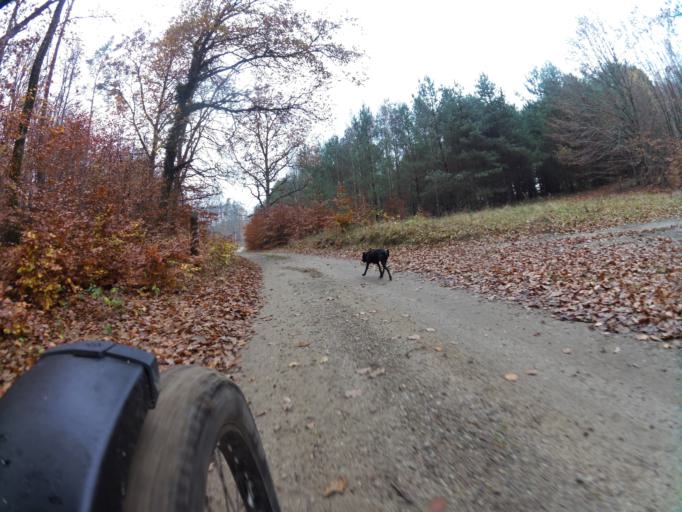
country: PL
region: Pomeranian Voivodeship
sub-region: Powiat pucki
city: Krokowa
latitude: 54.7145
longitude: 18.1408
